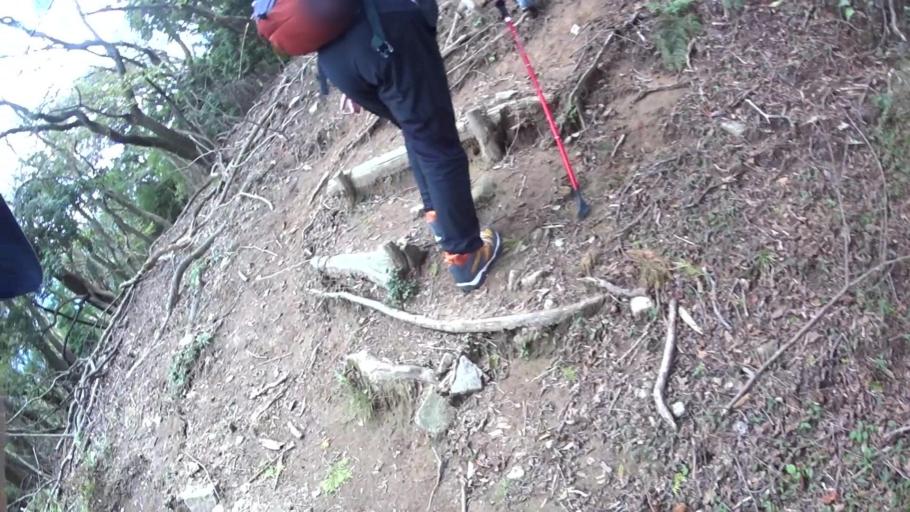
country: JP
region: Shiga Prefecture
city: Otsu-shi
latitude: 35.0947
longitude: 135.8375
